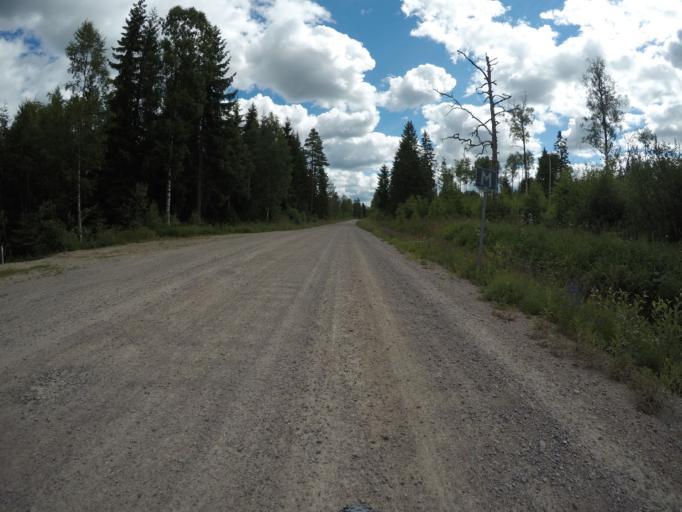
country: SE
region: Vaermland
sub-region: Filipstads Kommun
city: Lesjofors
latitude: 60.1310
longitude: 14.4181
